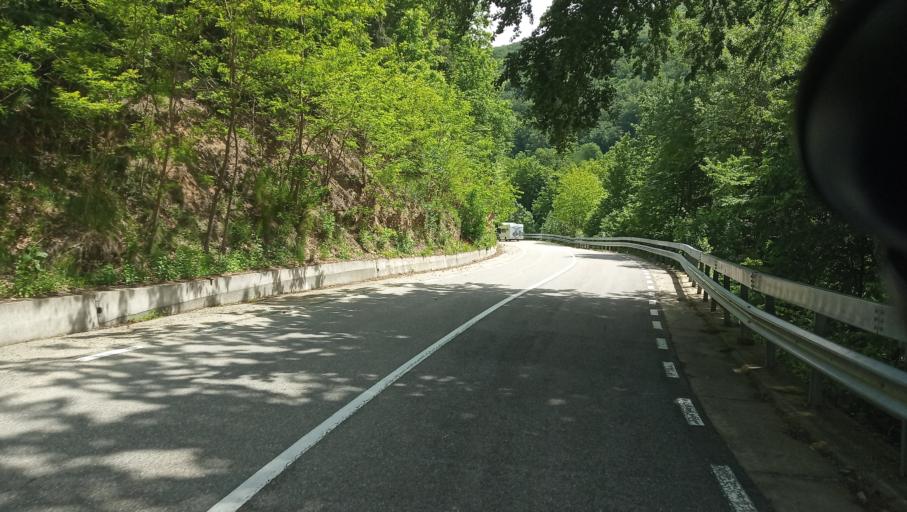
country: RO
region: Caras-Severin
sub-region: Comuna Brebu Nou
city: Brebu Nou
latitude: 45.2557
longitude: 22.1883
